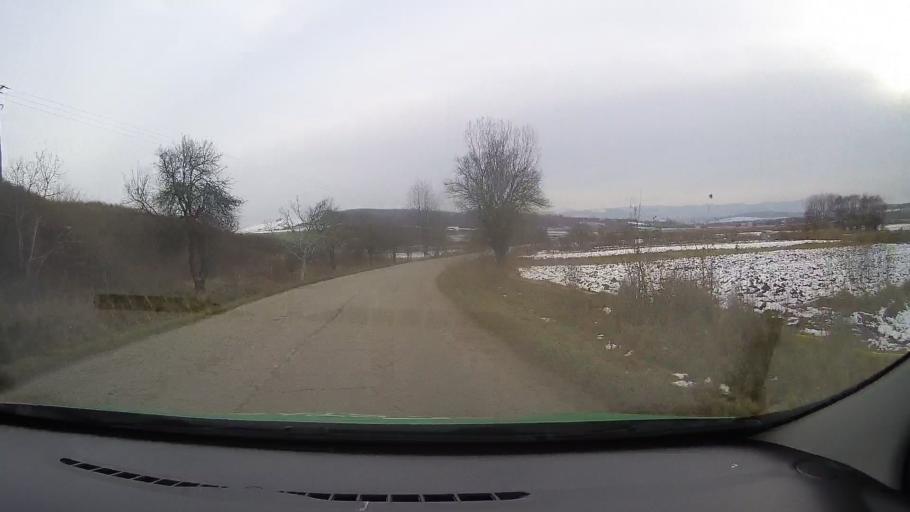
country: RO
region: Hunedoara
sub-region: Comuna Romos
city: Romos
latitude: 45.8658
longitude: 23.2728
